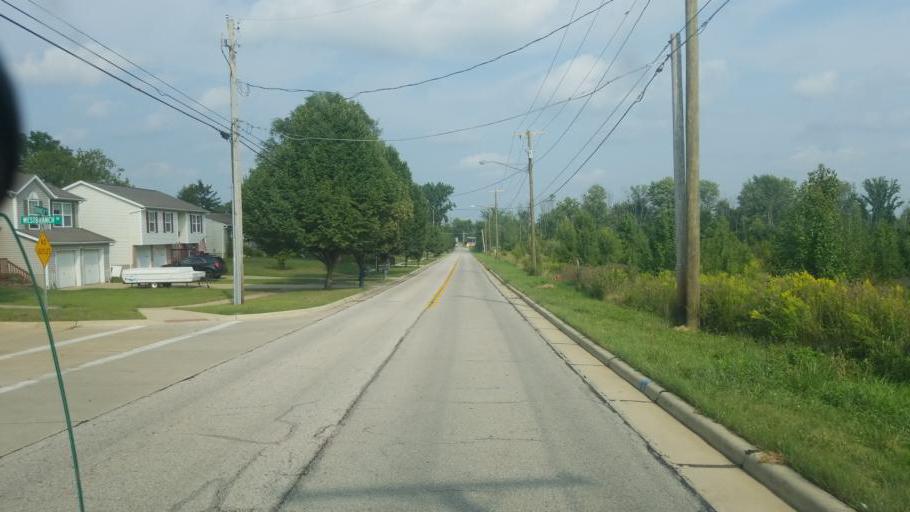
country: US
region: Ohio
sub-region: Medina County
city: Medina
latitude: 41.1425
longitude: -81.8918
